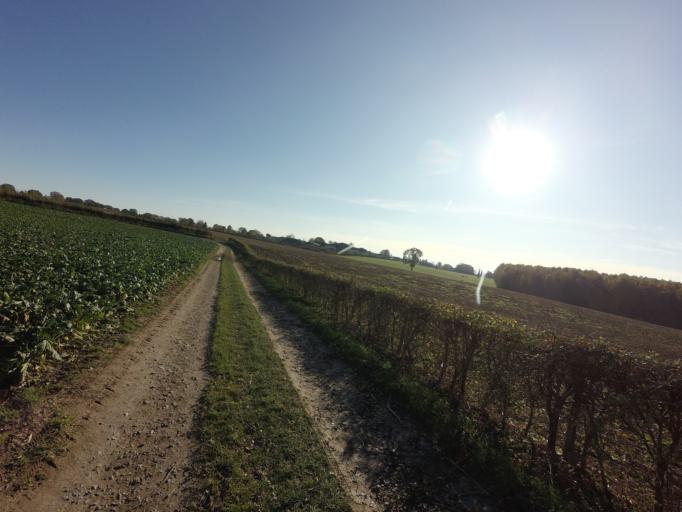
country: NL
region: Limburg
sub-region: Gemeente Simpelveld
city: Simpelveld
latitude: 50.8230
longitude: 5.9727
